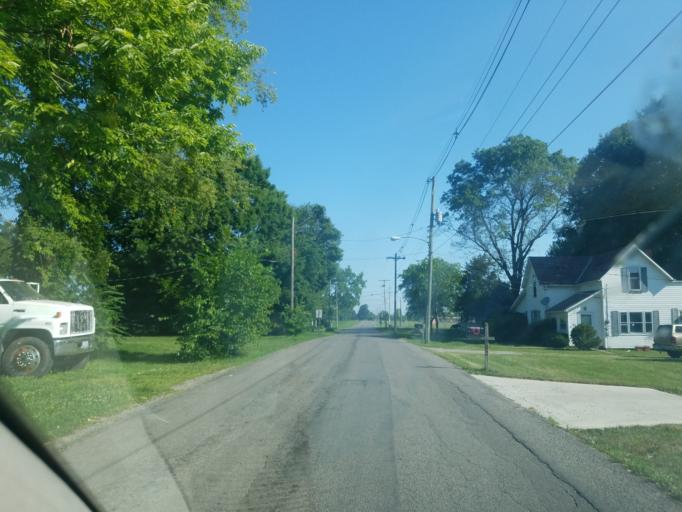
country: US
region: Ohio
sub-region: Union County
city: Richwood
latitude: 40.4322
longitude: -83.3027
